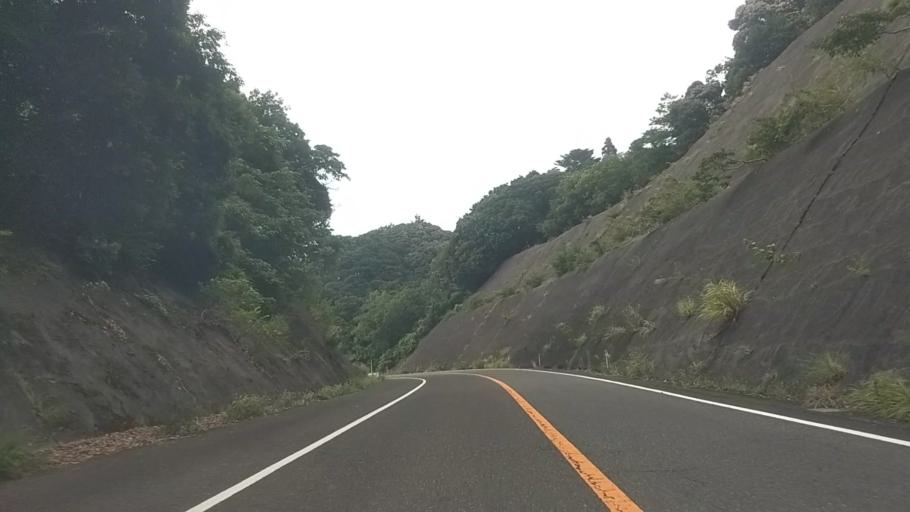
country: JP
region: Chiba
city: Kawaguchi
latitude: 35.2101
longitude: 140.0534
